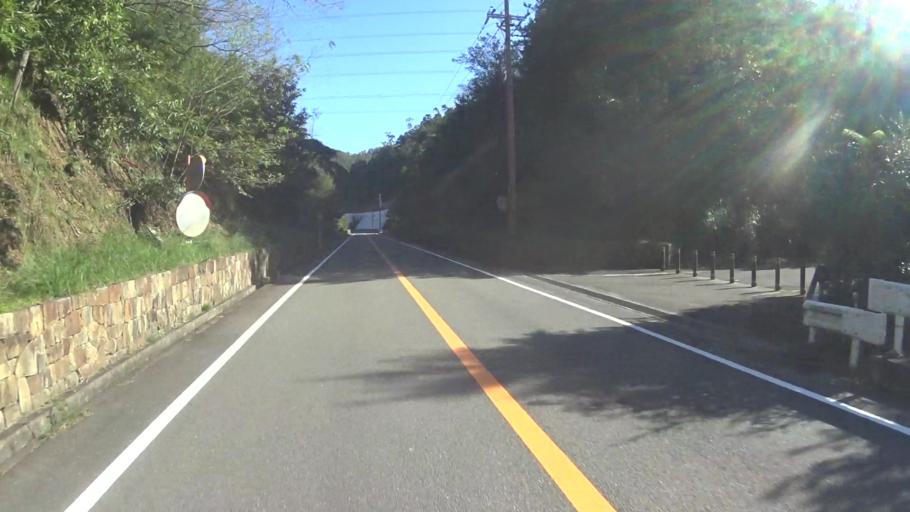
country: JP
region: Kyoto
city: Kameoka
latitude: 35.1366
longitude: 135.5338
